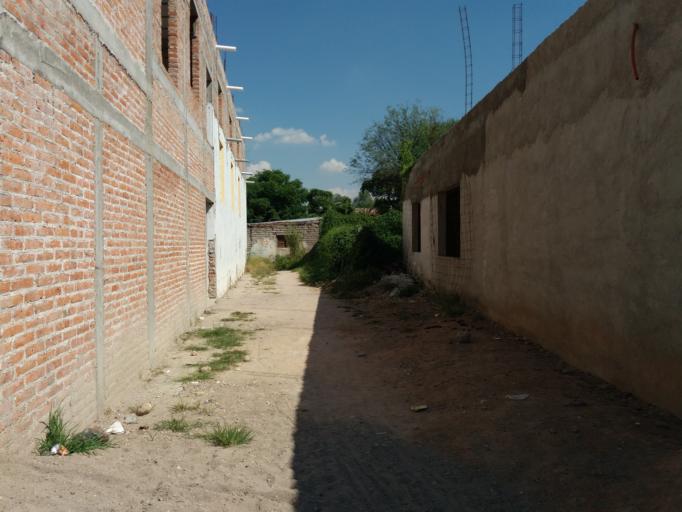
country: MX
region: Aguascalientes
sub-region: Aguascalientes
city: Penuelas (El Cienegal)
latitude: 21.7565
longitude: -102.3024
